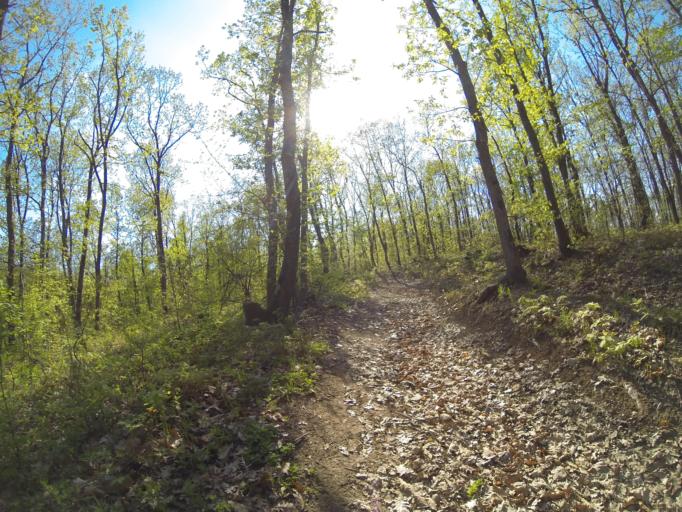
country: RO
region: Gorj
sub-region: Comuna Crusetu
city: Crusetu
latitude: 44.6228
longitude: 23.6307
